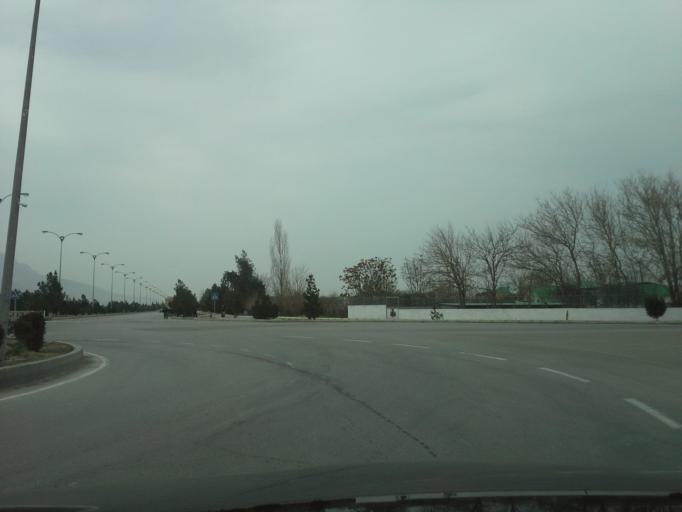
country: TM
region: Ahal
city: Abadan
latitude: 37.9770
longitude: 58.2455
